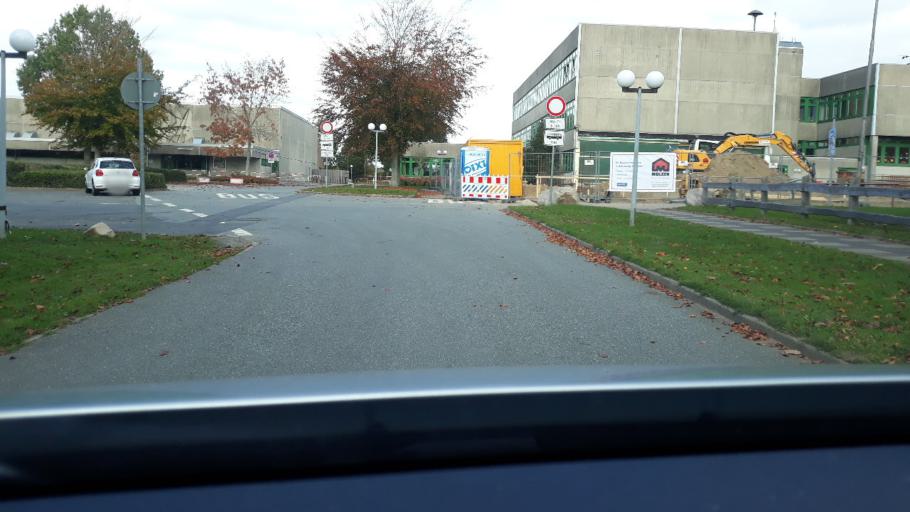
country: DE
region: Schleswig-Holstein
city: Boklund
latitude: 54.6026
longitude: 9.5753
